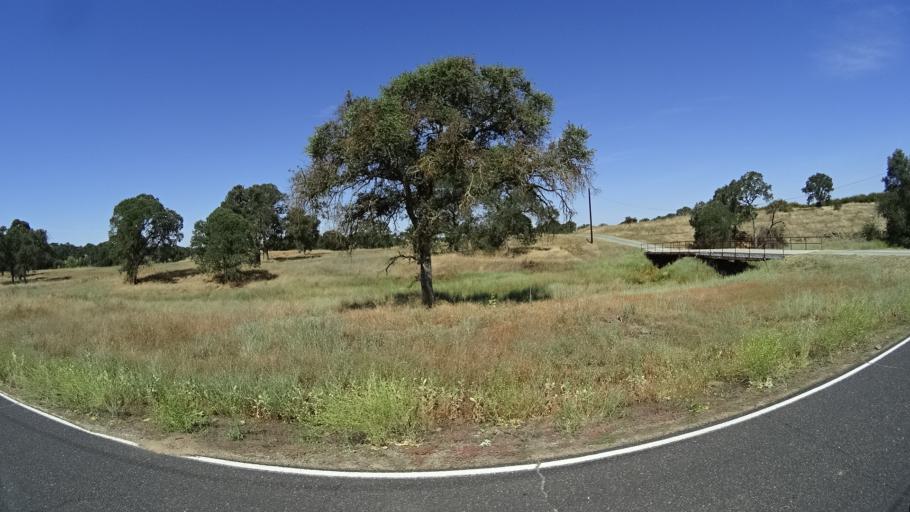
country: US
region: California
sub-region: Calaveras County
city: Rancho Calaveras
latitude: 38.1115
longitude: -120.9265
